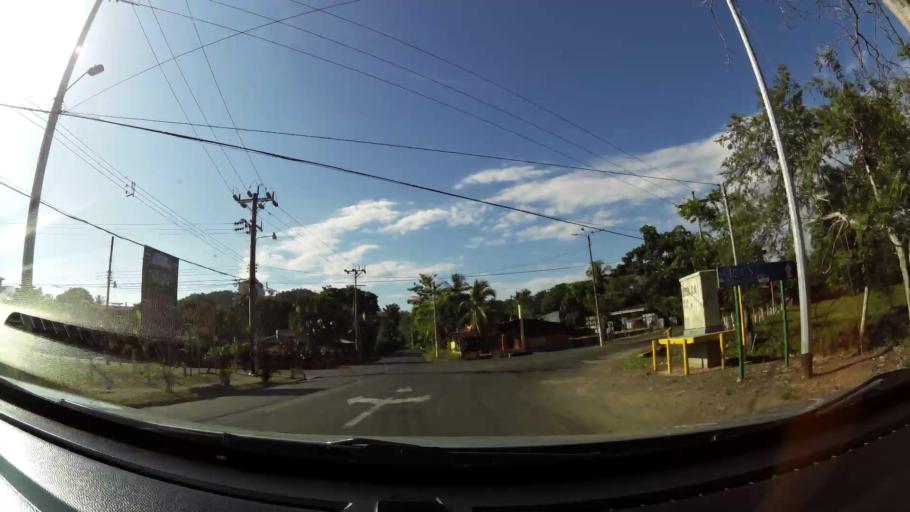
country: CR
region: Puntarenas
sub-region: Canton de Garabito
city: Jaco
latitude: 9.6219
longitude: -84.6369
